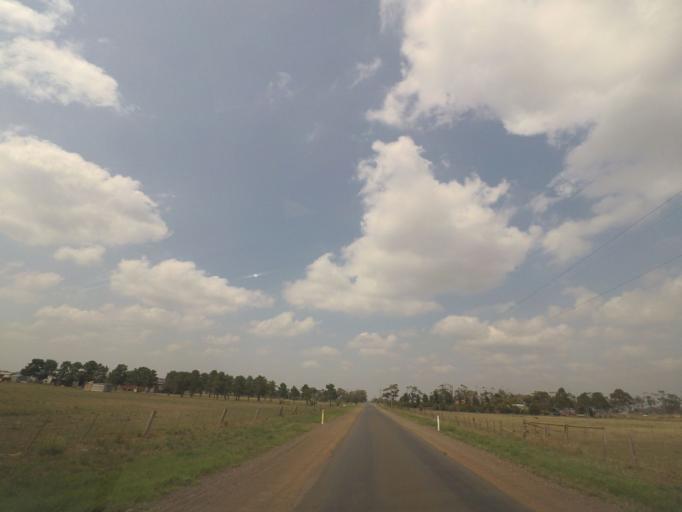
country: AU
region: Victoria
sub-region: Melton
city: Melton West
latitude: -37.6526
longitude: 144.5559
